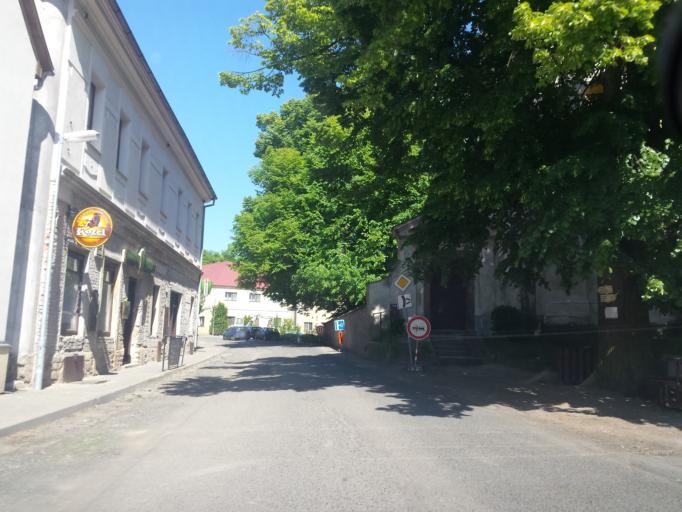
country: CZ
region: Central Bohemia
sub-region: Okres Melnik
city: Melnik
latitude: 50.4124
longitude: 14.5374
